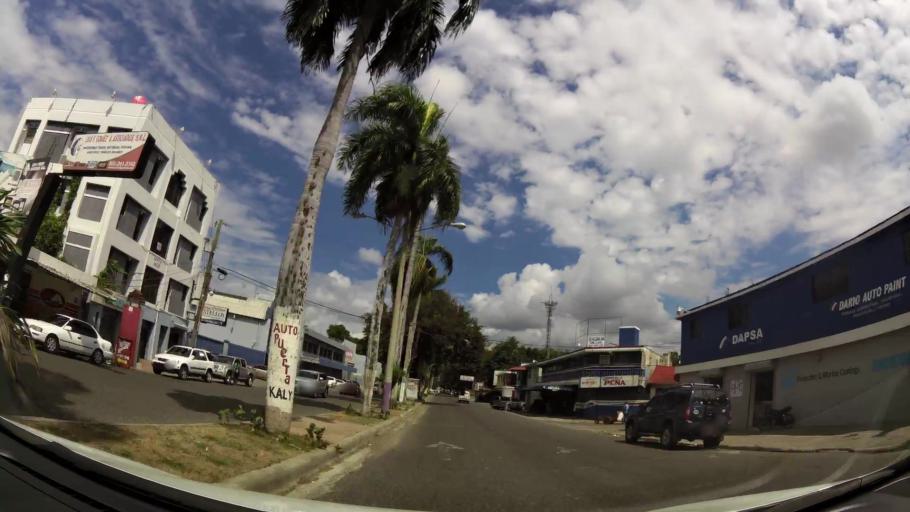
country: DO
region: Santiago
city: Santiago de los Caballeros
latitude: 19.4590
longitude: -70.7093
